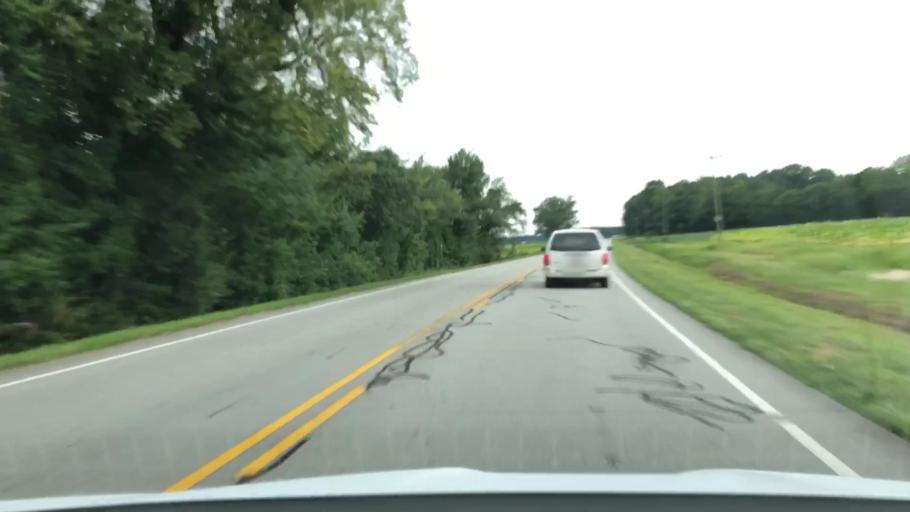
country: US
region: North Carolina
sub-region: Jones County
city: Trenton
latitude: 35.0784
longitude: -77.4243
